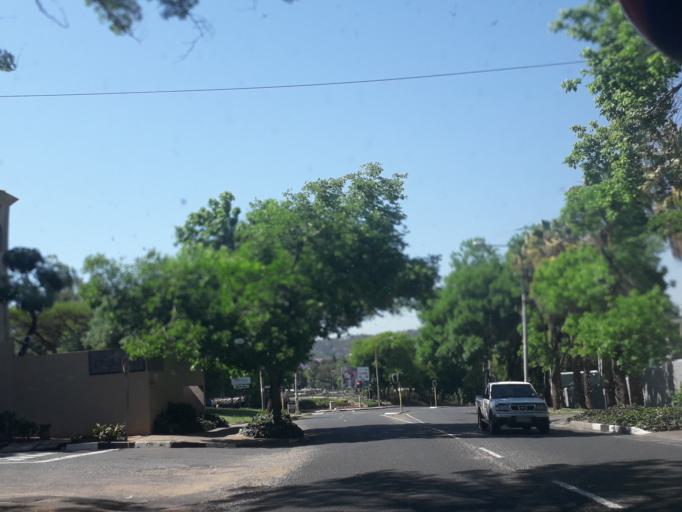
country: ZA
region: Gauteng
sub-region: City of Johannesburg Metropolitan Municipality
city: Johannesburg
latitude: -26.1456
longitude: 28.0774
